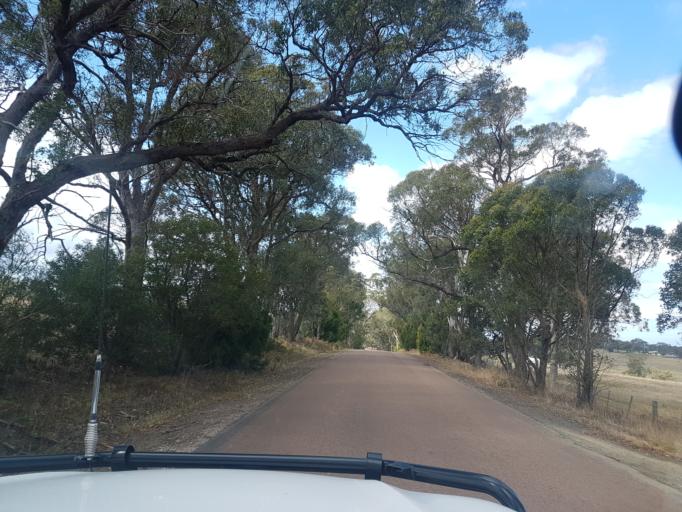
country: AU
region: Victoria
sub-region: East Gippsland
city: Bairnsdale
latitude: -37.7867
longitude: 147.5985
